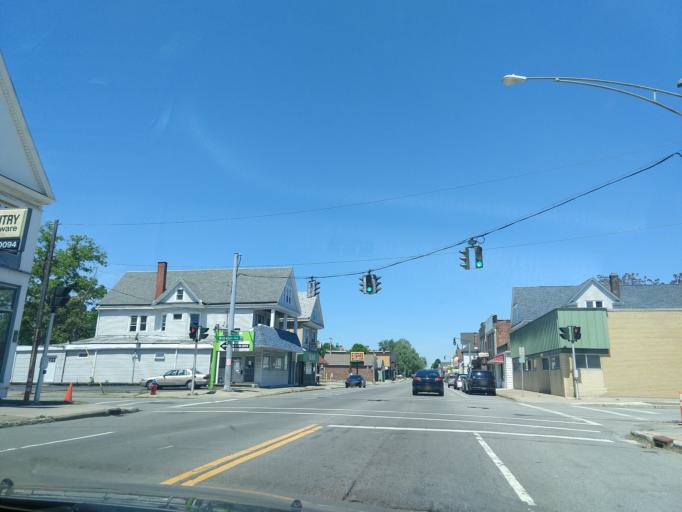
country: US
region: New York
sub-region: Erie County
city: West Seneca
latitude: 42.8471
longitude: -78.8001
